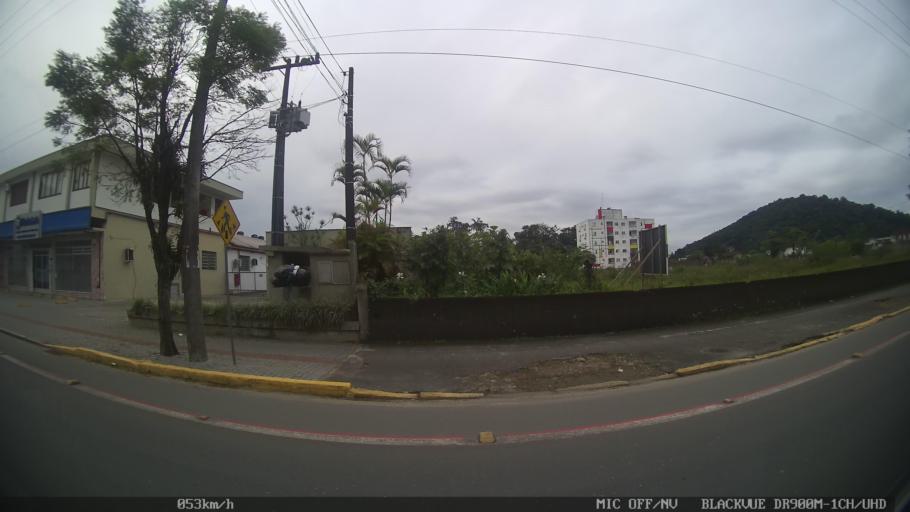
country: BR
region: Santa Catarina
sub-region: Joinville
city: Joinville
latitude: -26.2935
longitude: -48.8673
